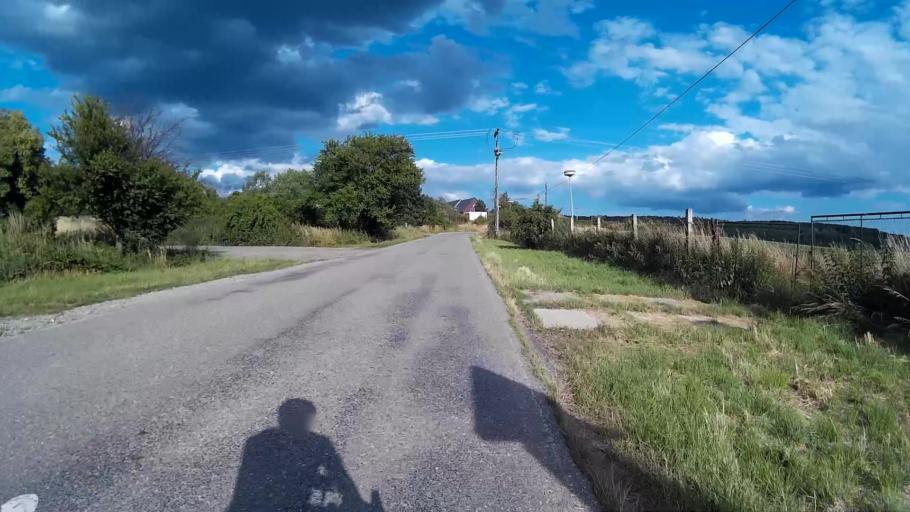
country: CZ
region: South Moravian
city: Ricany
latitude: 49.2062
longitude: 16.4254
